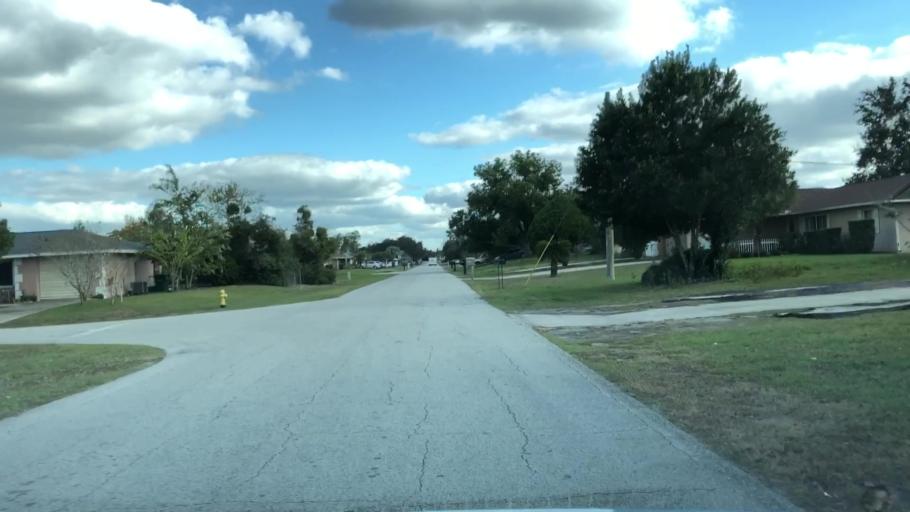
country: US
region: Florida
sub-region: Volusia County
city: Deltona
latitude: 28.8804
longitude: -81.2408
